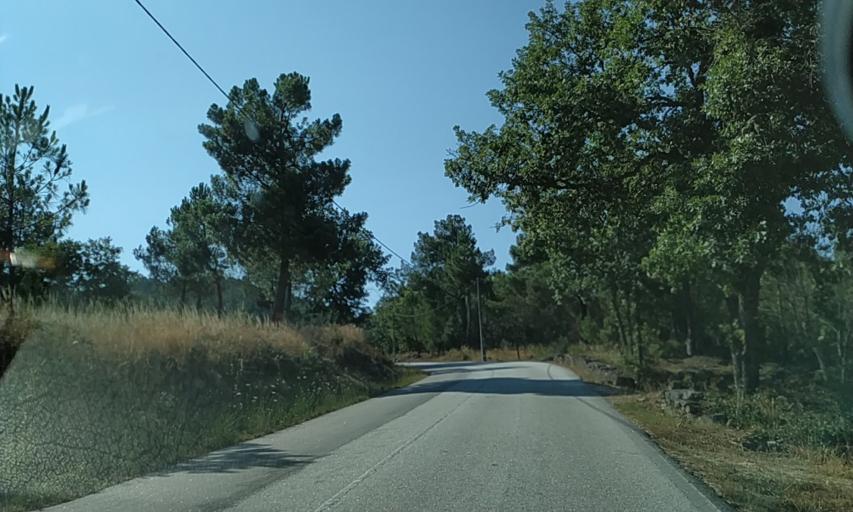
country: PT
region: Viseu
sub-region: Moimenta da Beira
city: Moimenta da Beira
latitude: 41.0004
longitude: -7.5605
